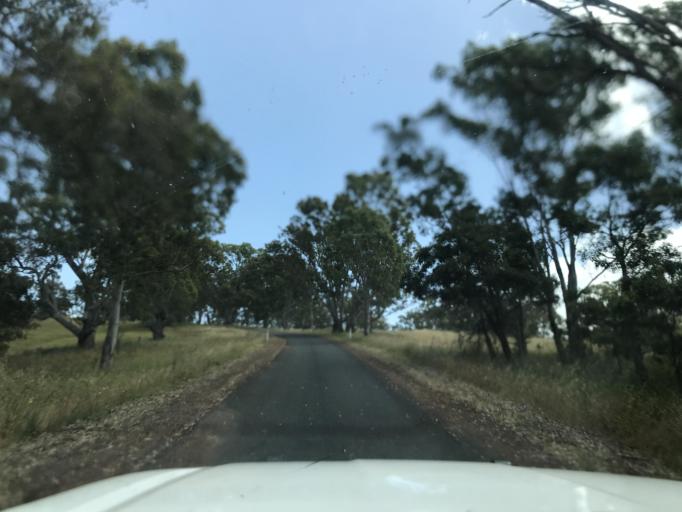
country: AU
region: South Australia
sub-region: Wattle Range
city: Penola
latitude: -37.2669
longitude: 141.5134
